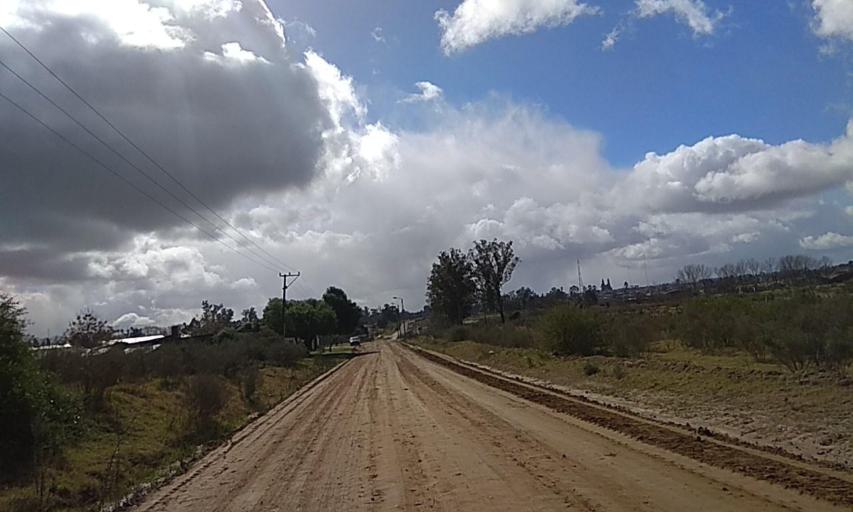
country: UY
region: Florida
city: Florida
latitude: -34.1155
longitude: -56.2283
